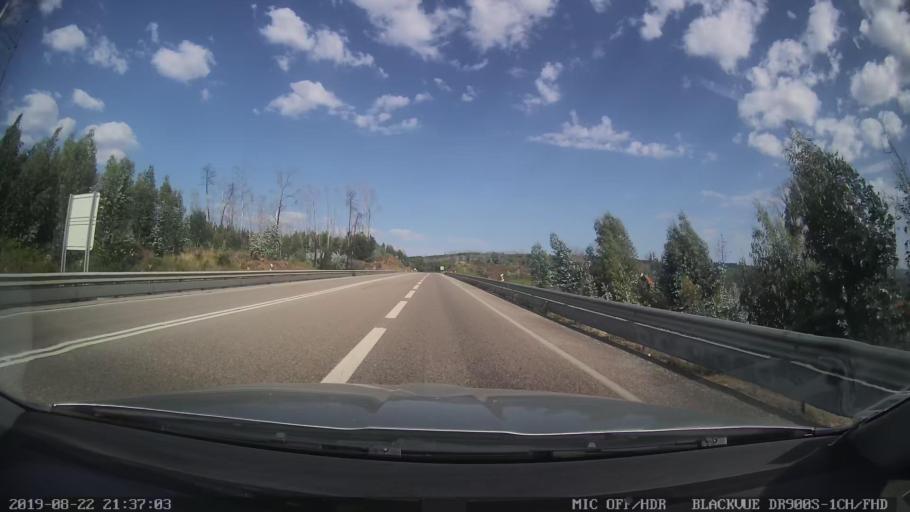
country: PT
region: Leiria
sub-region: Figueiro Dos Vinhos
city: Figueiro dos Vinhos
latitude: 39.9284
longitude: -8.2403
